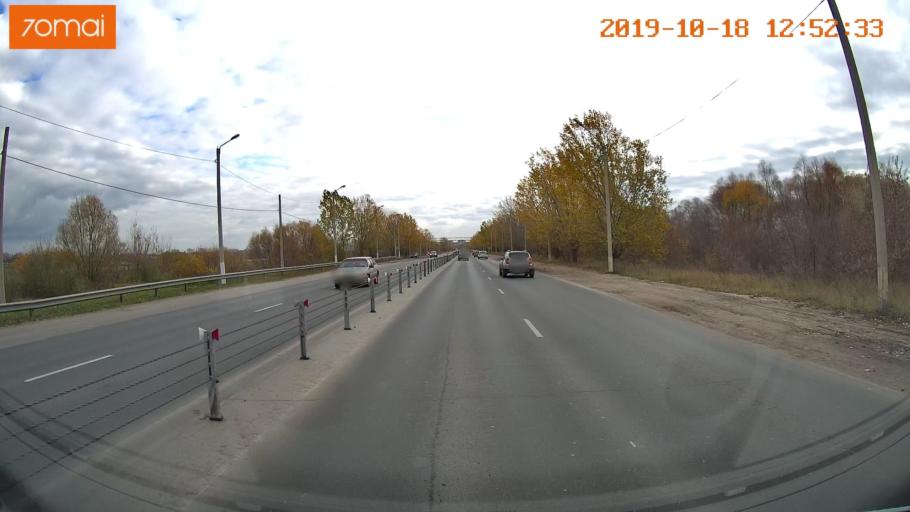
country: RU
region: Rjazan
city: Ryazan'
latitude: 54.6514
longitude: 39.6952
